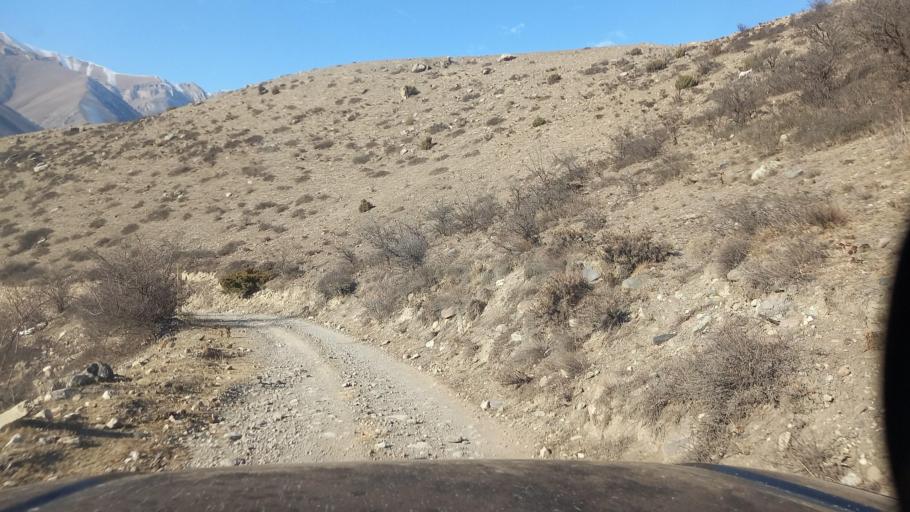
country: RU
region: Ingushetiya
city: Dzhayrakh
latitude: 42.8460
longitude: 44.6539
